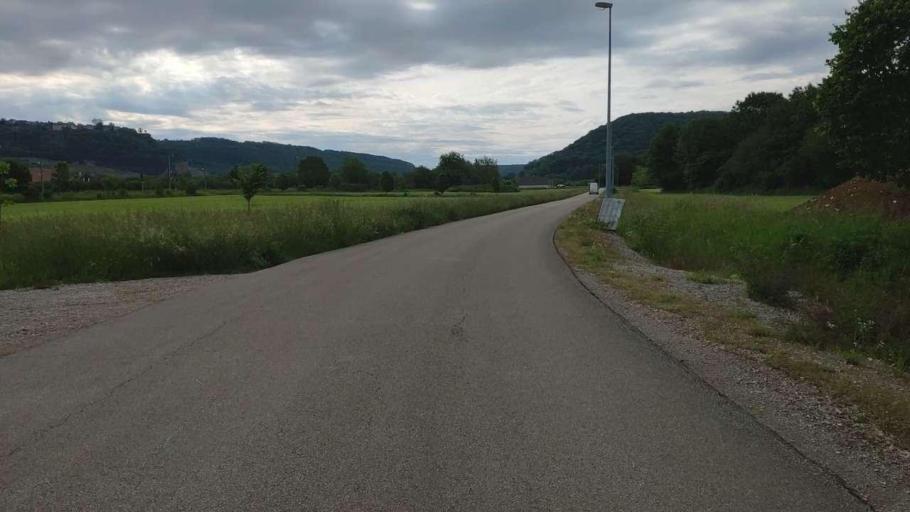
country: FR
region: Franche-Comte
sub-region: Departement du Jura
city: Perrigny
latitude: 46.7573
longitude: 5.5994
